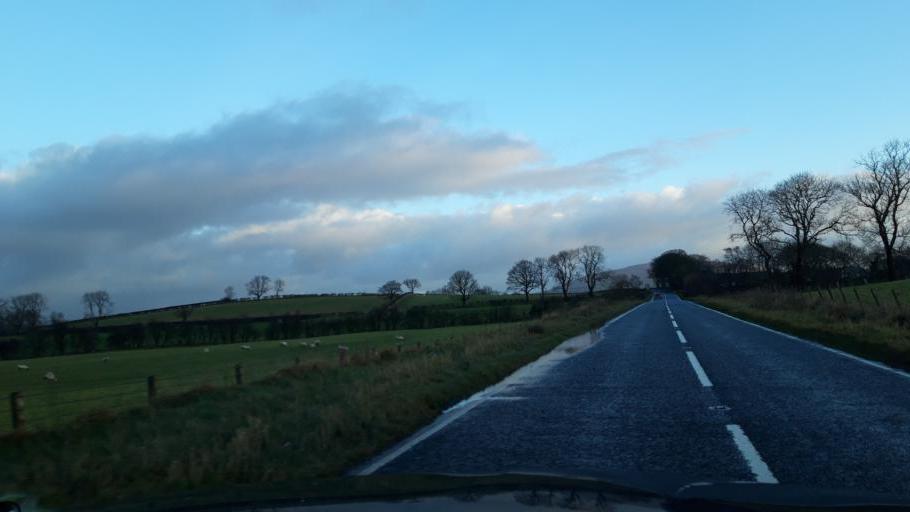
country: GB
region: Northern Ireland
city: Dunloy
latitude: 55.1046
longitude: -6.3464
